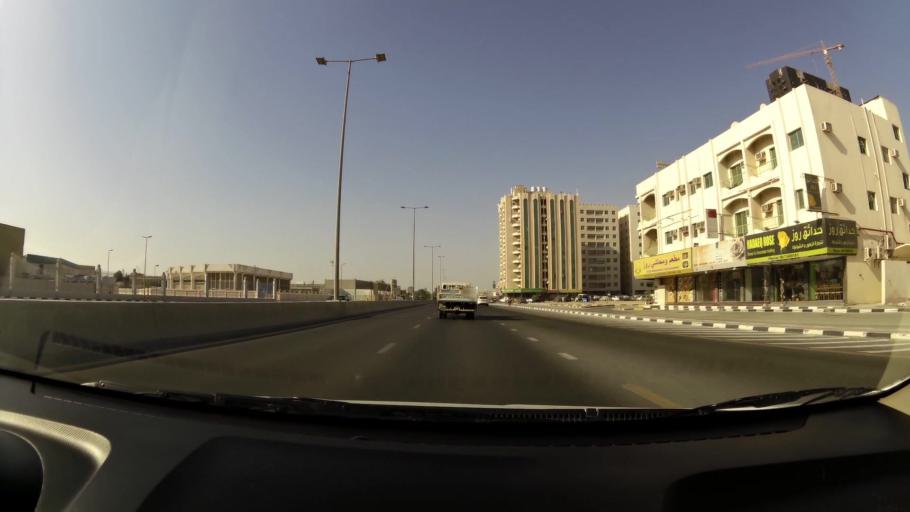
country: AE
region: Ajman
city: Ajman
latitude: 25.3955
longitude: 55.4717
